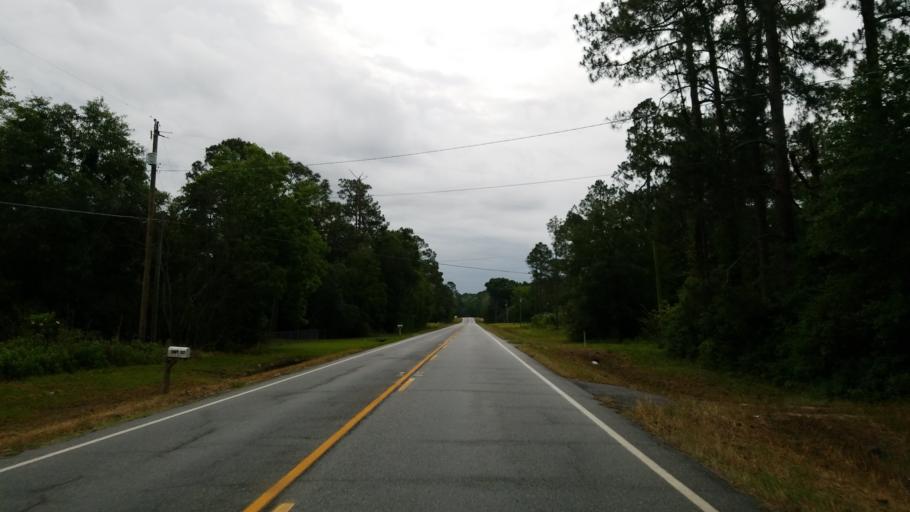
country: US
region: Georgia
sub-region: Berrien County
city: Ray City
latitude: 31.0766
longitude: -83.2177
